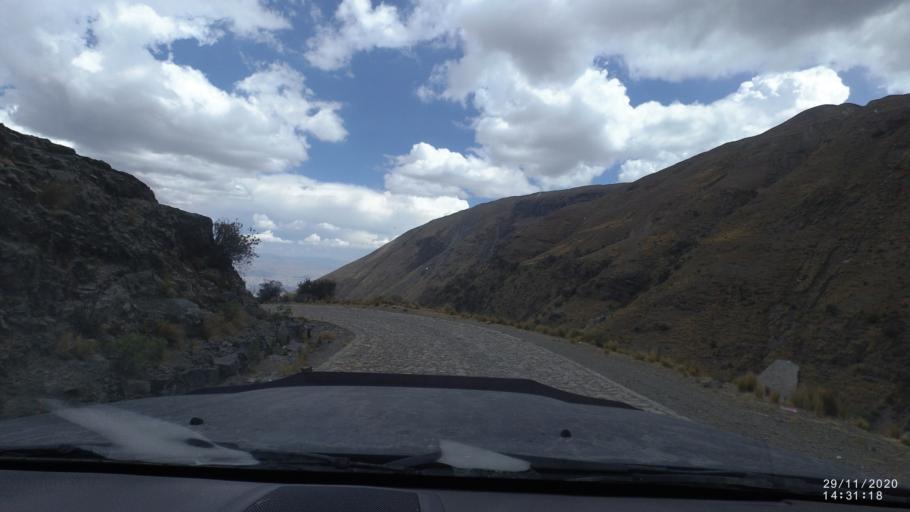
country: BO
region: Cochabamba
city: Sipe Sipe
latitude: -17.2663
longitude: -66.3452
